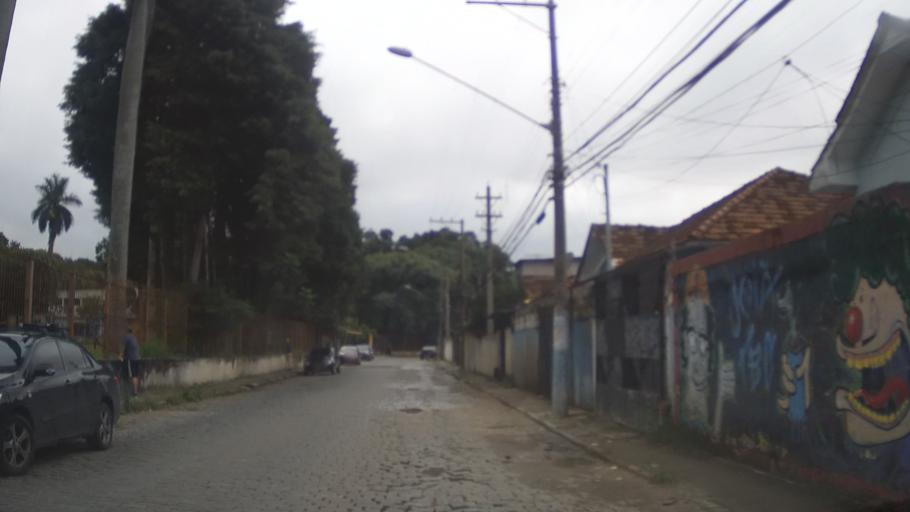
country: BR
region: Sao Paulo
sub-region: Guarulhos
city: Guarulhos
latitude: -23.4673
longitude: -46.5493
